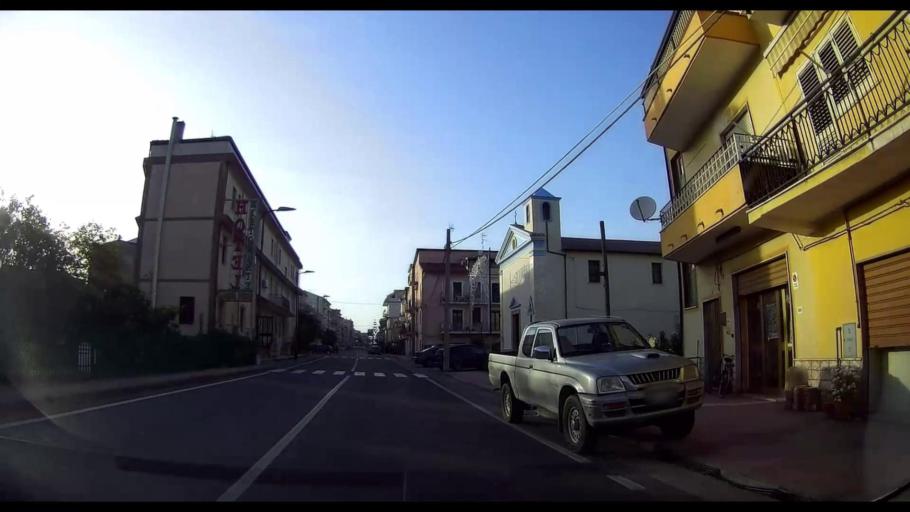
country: IT
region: Calabria
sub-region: Provincia di Crotone
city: Torretta
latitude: 39.4515
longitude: 17.0383
